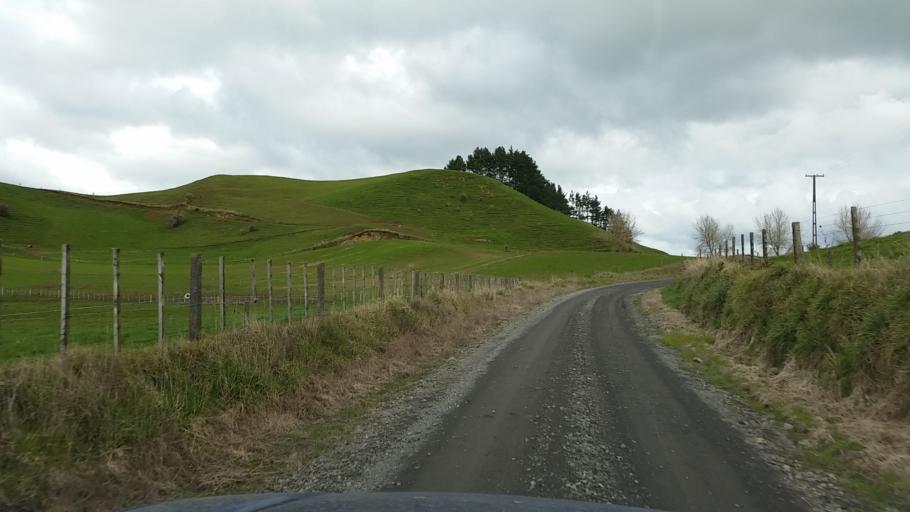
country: NZ
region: Taranaki
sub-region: South Taranaki District
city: Eltham
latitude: -39.3540
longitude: 174.3845
